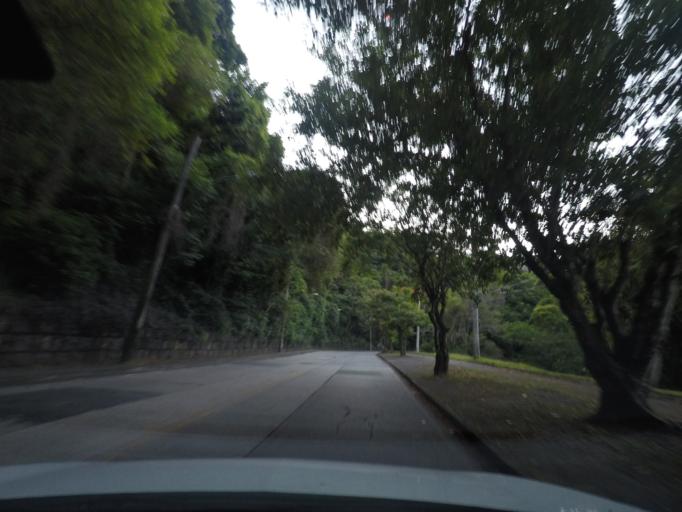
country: BR
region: Rio de Janeiro
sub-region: Rio De Janeiro
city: Rio de Janeiro
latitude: -22.9581
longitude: -43.2645
